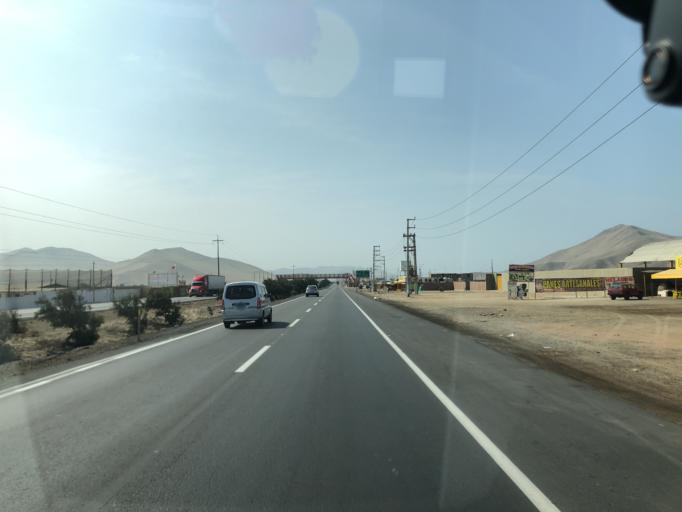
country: PE
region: Lima
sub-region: Provincia de Canete
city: Chilca
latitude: -12.5375
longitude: -76.7192
